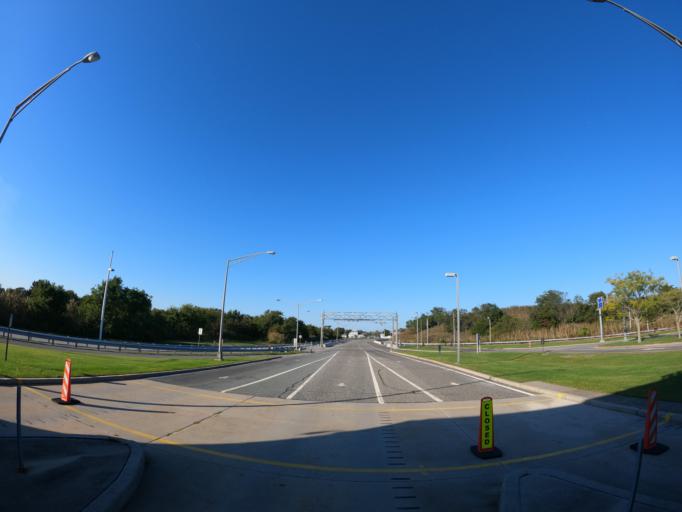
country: US
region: New Jersey
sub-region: Cape May County
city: North Cape May
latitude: 38.9710
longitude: -74.9587
